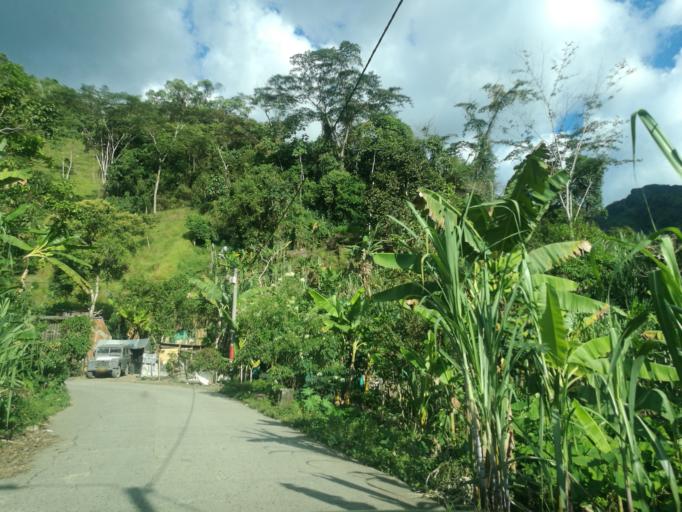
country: CO
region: Boyaca
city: Maripi
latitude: 5.5497
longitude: -74.0015
